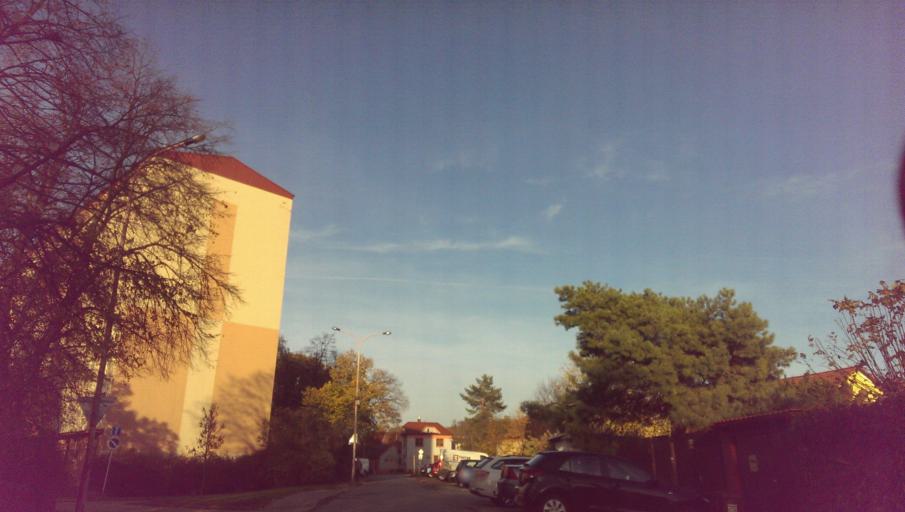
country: CZ
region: Zlin
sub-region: Okres Uherske Hradiste
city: Uherske Hradiste
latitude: 49.0668
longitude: 17.4757
